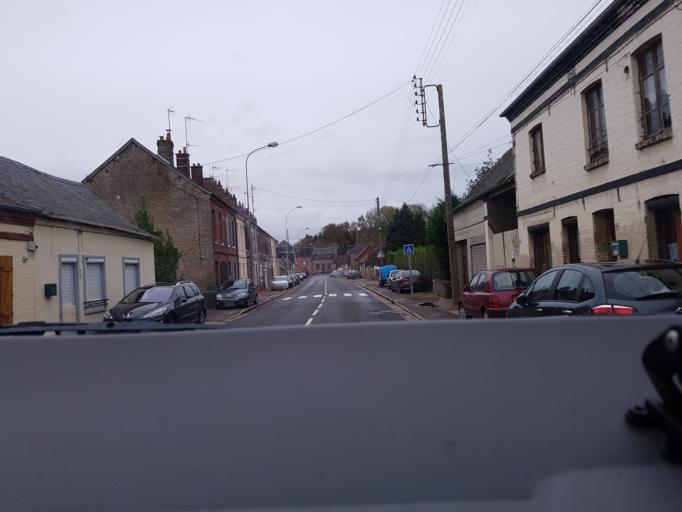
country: FR
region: Picardie
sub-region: Departement de la Somme
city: Abbeville
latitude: 50.1054
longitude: 1.7964
